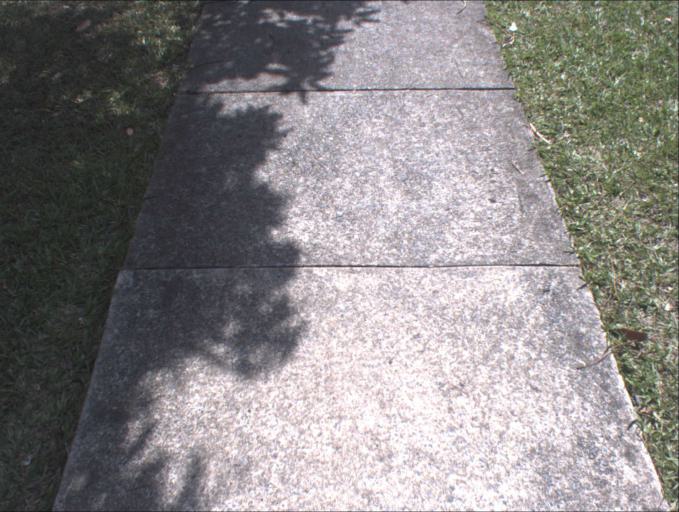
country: AU
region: Queensland
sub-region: Logan
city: Woodridge
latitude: -27.6296
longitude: 153.0987
